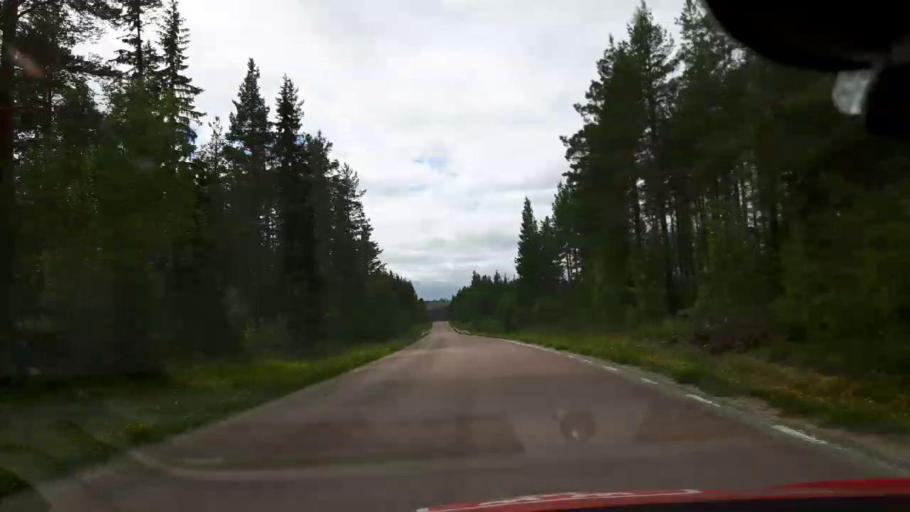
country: SE
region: Jaemtland
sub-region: Braecke Kommun
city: Braecke
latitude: 62.9064
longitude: 15.1547
